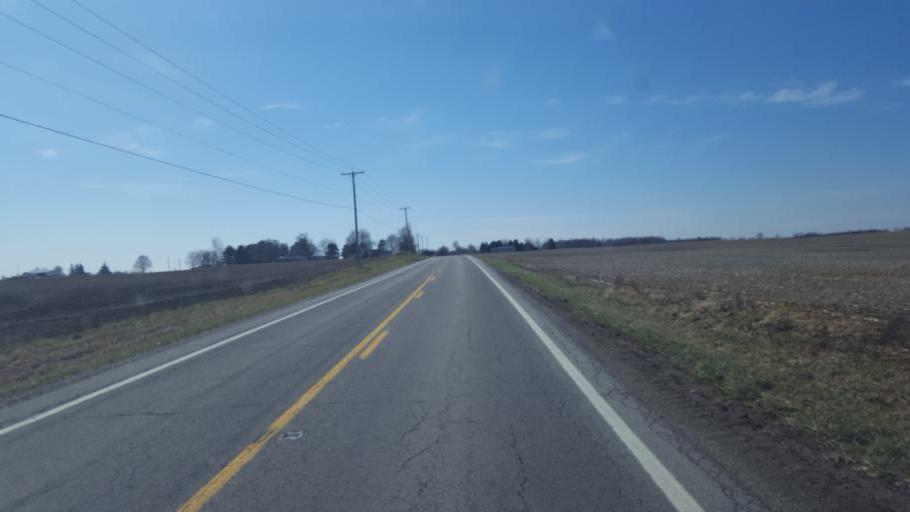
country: US
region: Ohio
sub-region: Marion County
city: Prospect
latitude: 40.5283
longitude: -83.2206
